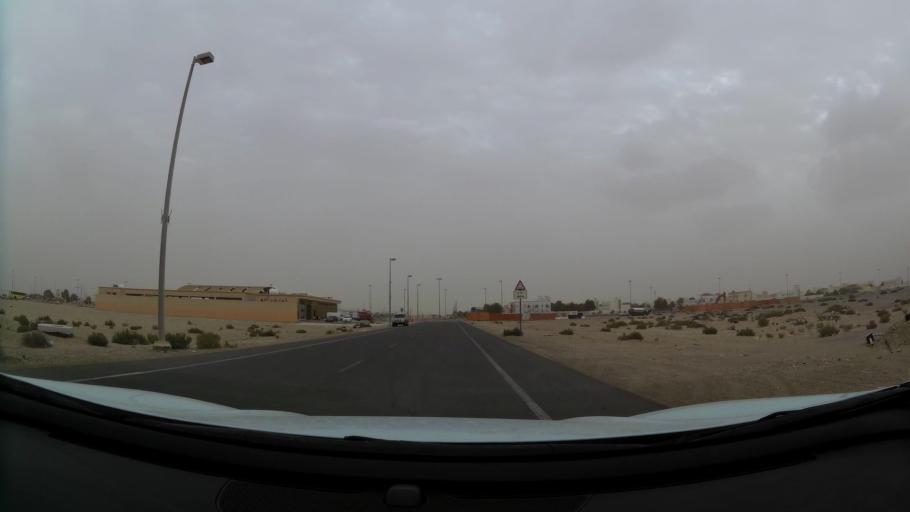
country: AE
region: Abu Dhabi
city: Abu Dhabi
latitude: 24.4234
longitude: 54.7295
